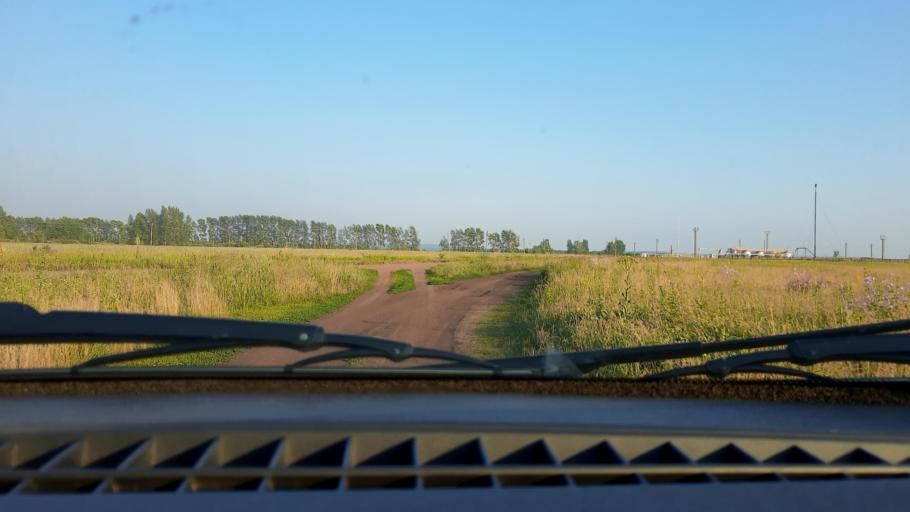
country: RU
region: Bashkortostan
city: Asanovo
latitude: 54.9373
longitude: 55.6226
